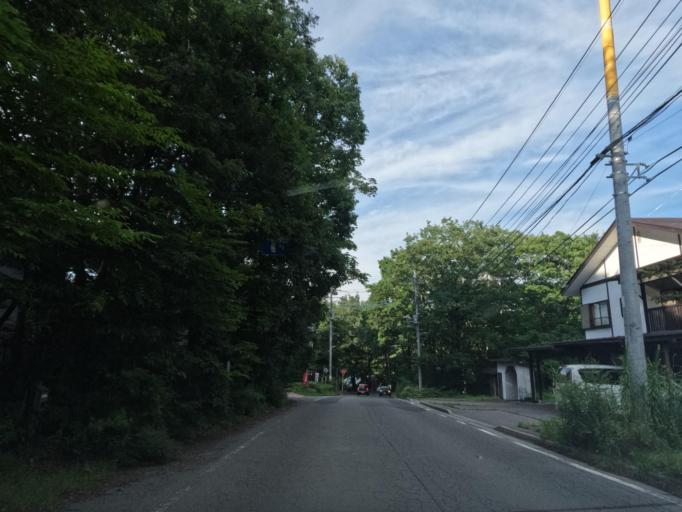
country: JP
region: Nagano
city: Komoro
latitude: 36.4695
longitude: 138.5644
